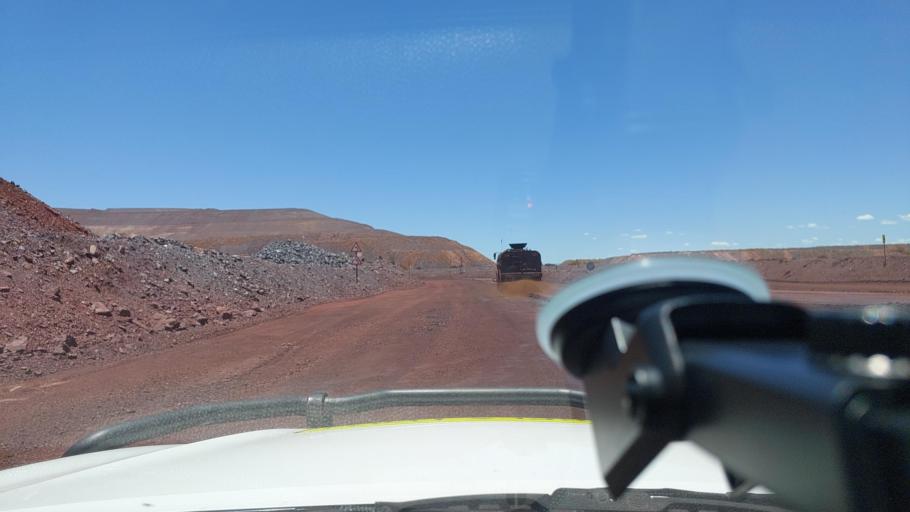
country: ZA
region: Northern Cape
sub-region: John Taolo Gaetsewe District Municipality
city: Kathu
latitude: -27.7616
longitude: 23.0091
